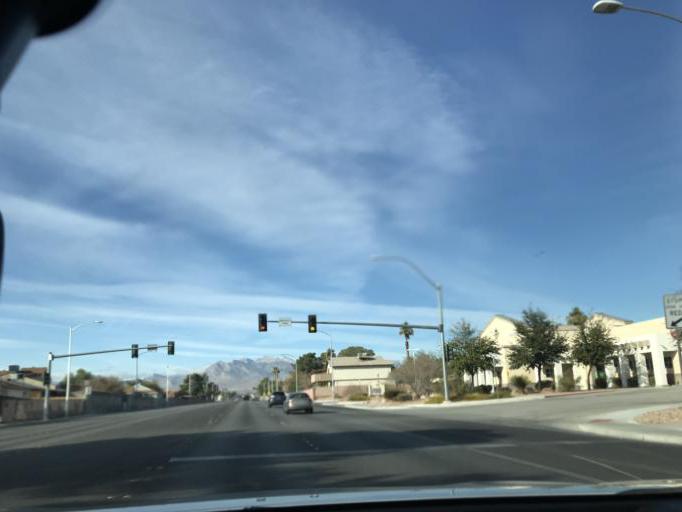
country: US
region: Nevada
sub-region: Clark County
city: Spring Valley
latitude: 36.2033
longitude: -115.2334
